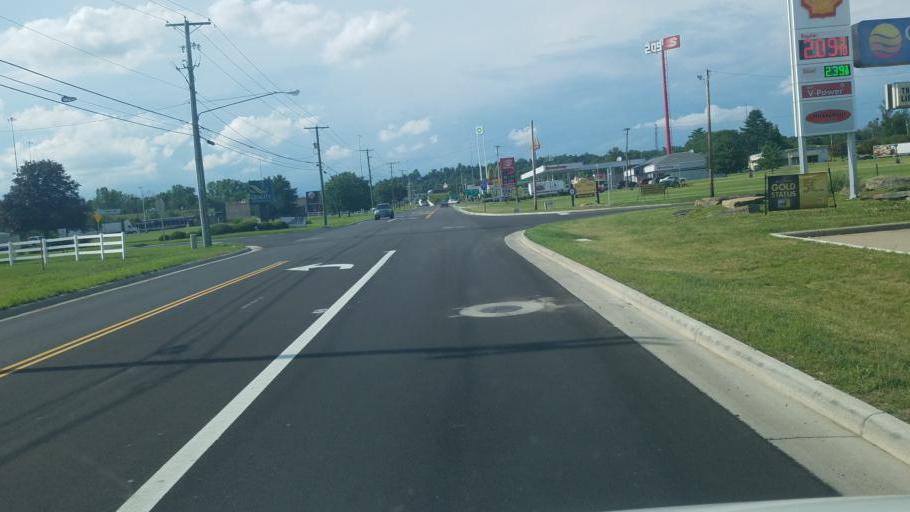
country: US
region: Ohio
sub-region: Sandusky County
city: Bellville
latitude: 40.6461
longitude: -82.5435
